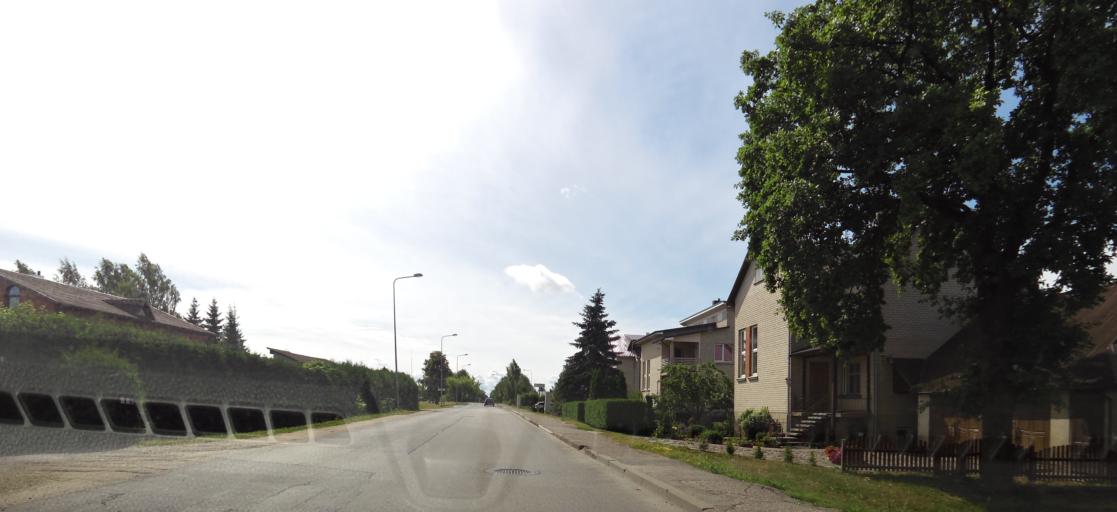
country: LT
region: Panevezys
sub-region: Birzai
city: Birzai
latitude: 56.1958
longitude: 24.7704
